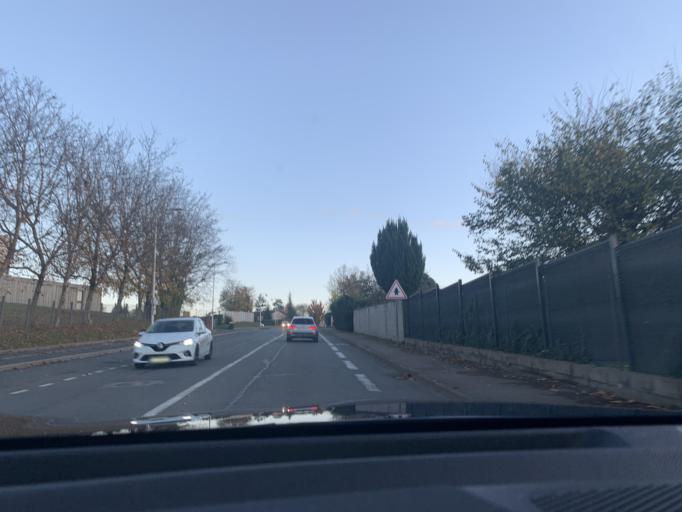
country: FR
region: Rhone-Alpes
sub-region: Departement du Rhone
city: Limas
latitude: 45.9793
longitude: 4.6991
